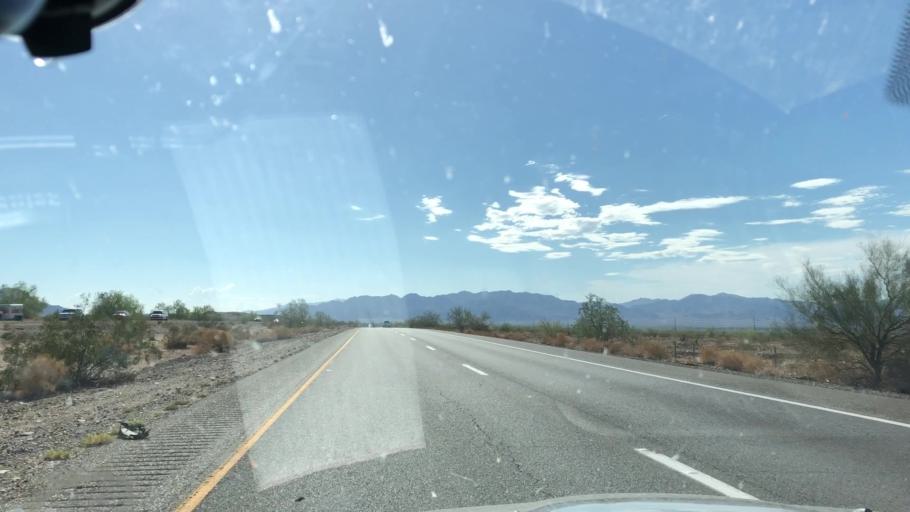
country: US
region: California
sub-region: Imperial County
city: Niland
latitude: 33.7051
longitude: -115.3346
